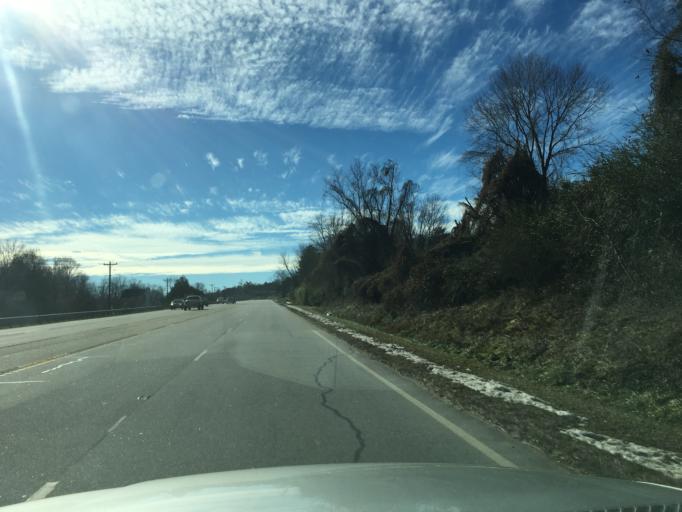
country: US
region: North Carolina
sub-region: Henderson County
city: Mills River
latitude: 35.3690
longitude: -82.5911
